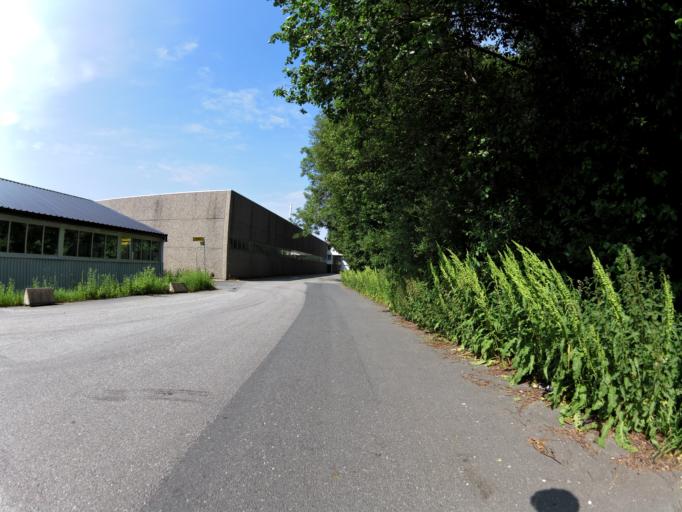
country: NO
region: Ostfold
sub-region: Sarpsborg
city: Sarpsborg
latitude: 59.2704
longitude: 11.1261
